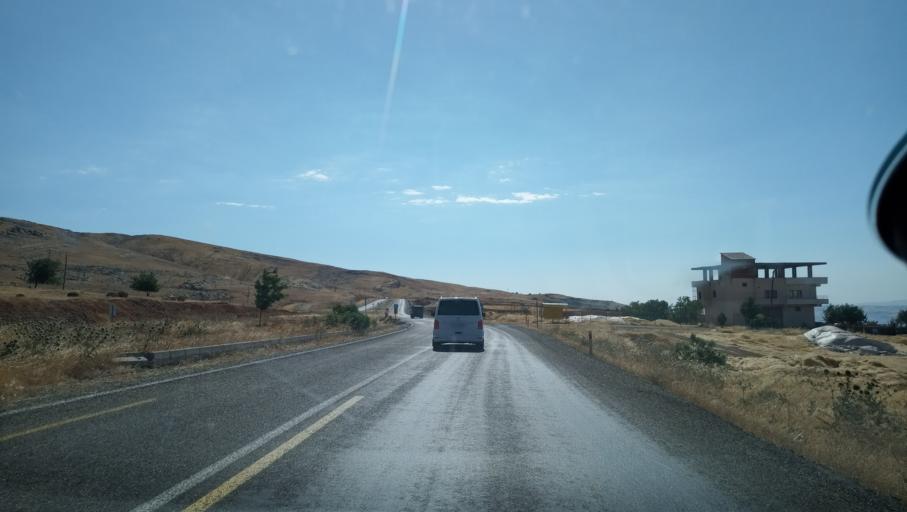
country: TR
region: Diyarbakir
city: Silvan
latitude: 38.1278
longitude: 41.0778
